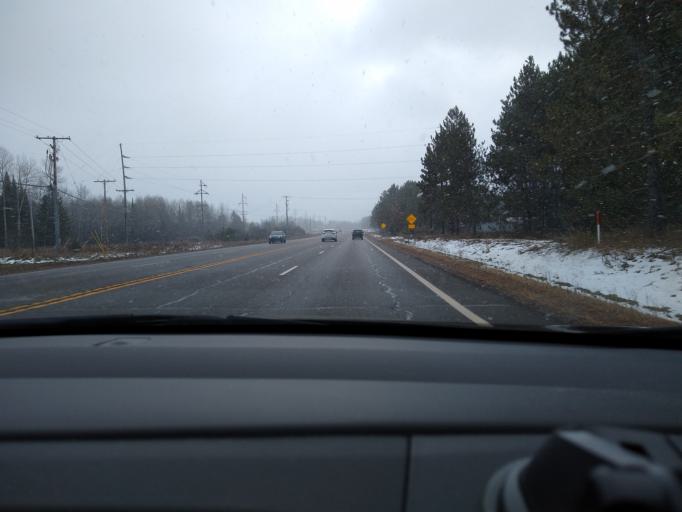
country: US
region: Michigan
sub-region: Dickinson County
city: Iron Mountain
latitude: 46.0427
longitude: -88.0614
